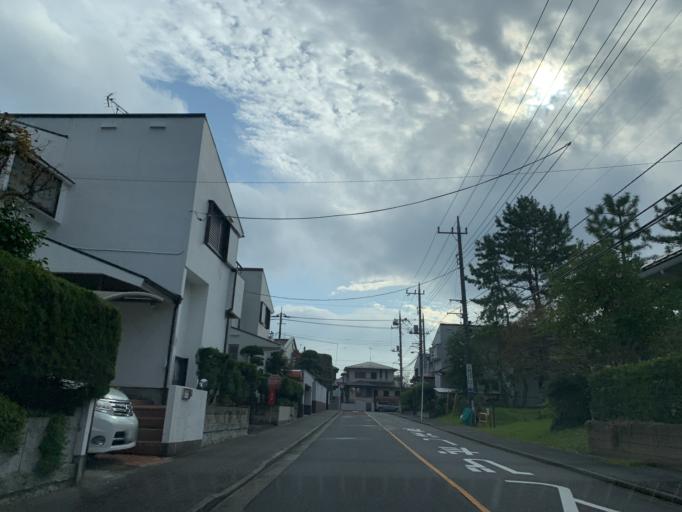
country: JP
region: Chiba
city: Nagareyama
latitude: 35.9035
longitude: 139.9145
